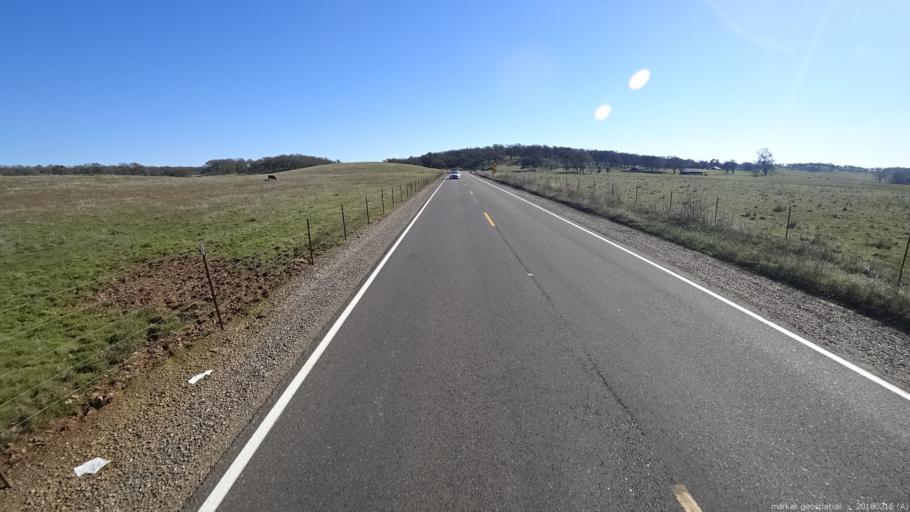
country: US
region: California
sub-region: Sacramento County
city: Rancho Murieta
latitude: 38.5460
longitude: -121.1112
